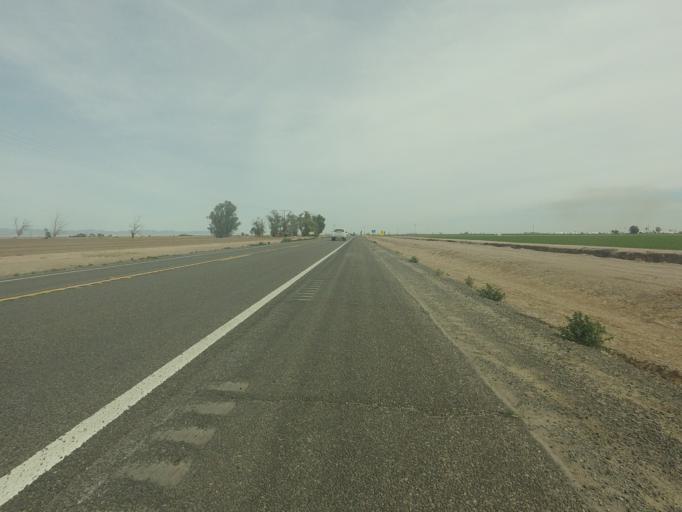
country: US
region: California
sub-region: Imperial County
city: Brawley
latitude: 32.9745
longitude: -115.4530
